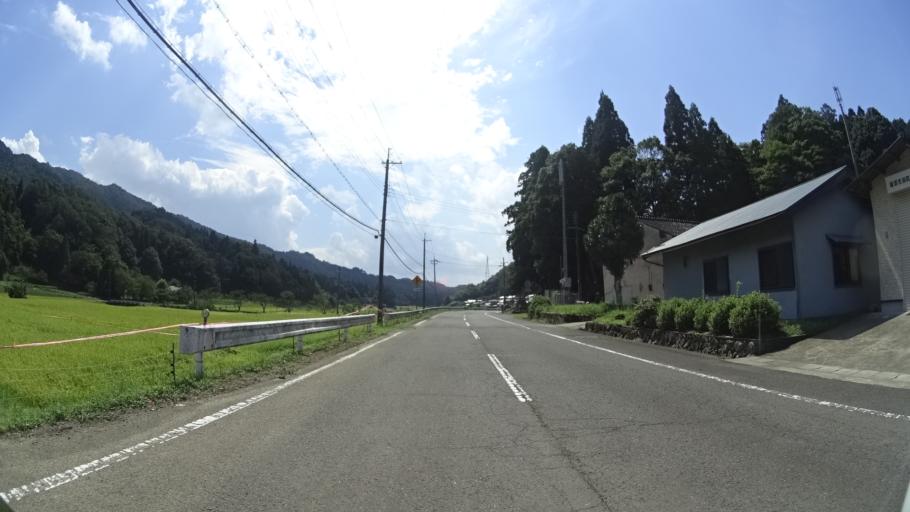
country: JP
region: Kyoto
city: Maizuru
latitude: 35.3734
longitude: 135.3423
